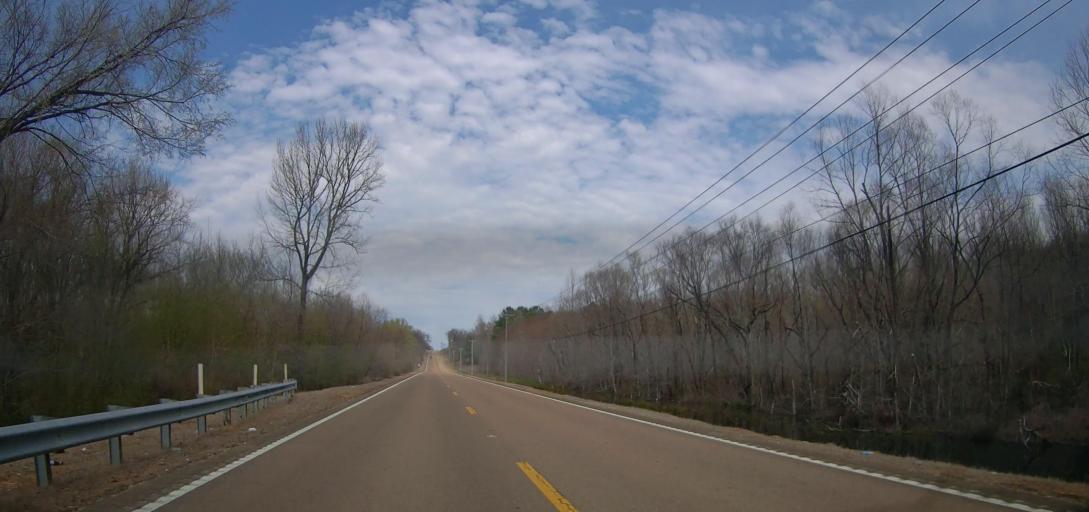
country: US
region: Mississippi
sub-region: Marshall County
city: Holly Springs
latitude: 34.7296
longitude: -89.4193
